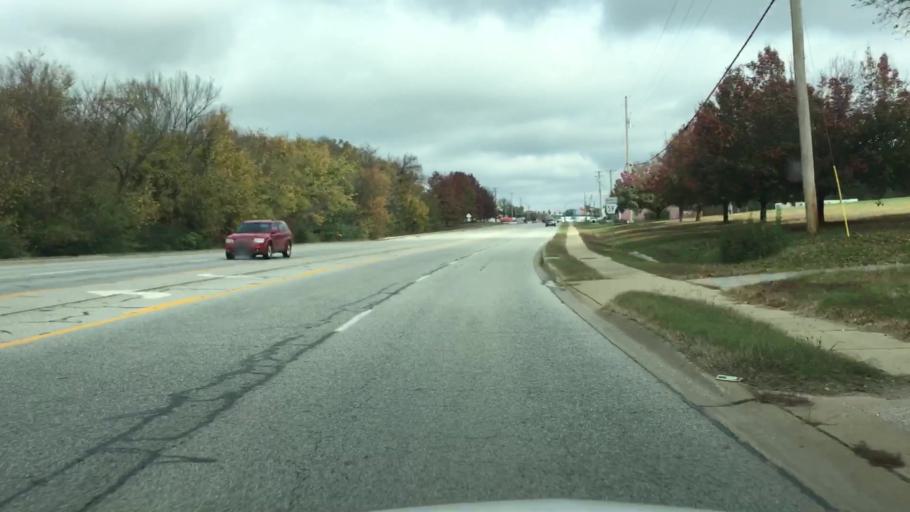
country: US
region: Arkansas
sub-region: Benton County
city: Gentry
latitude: 36.2603
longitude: -94.4845
